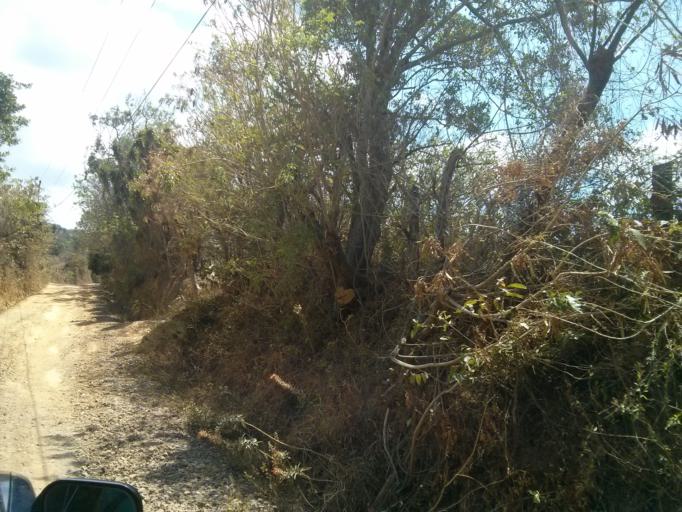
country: CR
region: Heredia
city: Colon
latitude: 9.9216
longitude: -84.2174
